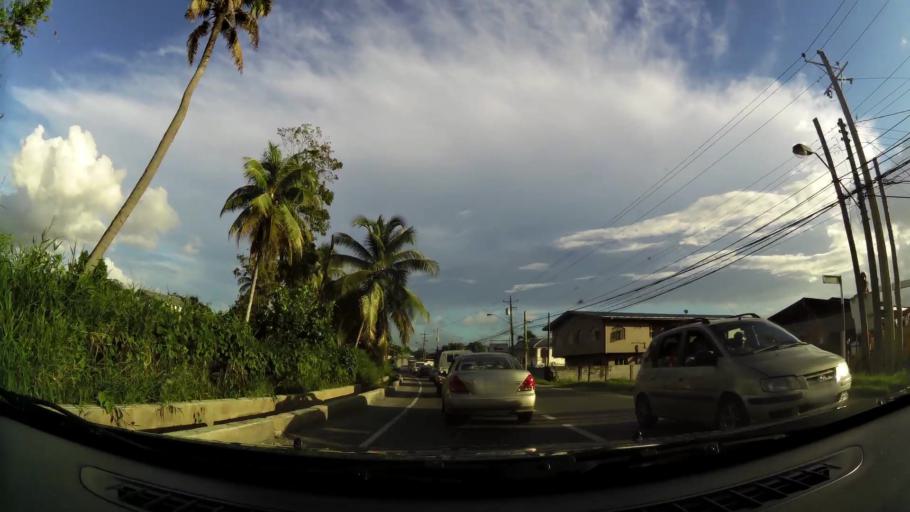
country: TT
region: Tunapuna/Piarco
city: Tunapuna
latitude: 10.5916
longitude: -61.3667
